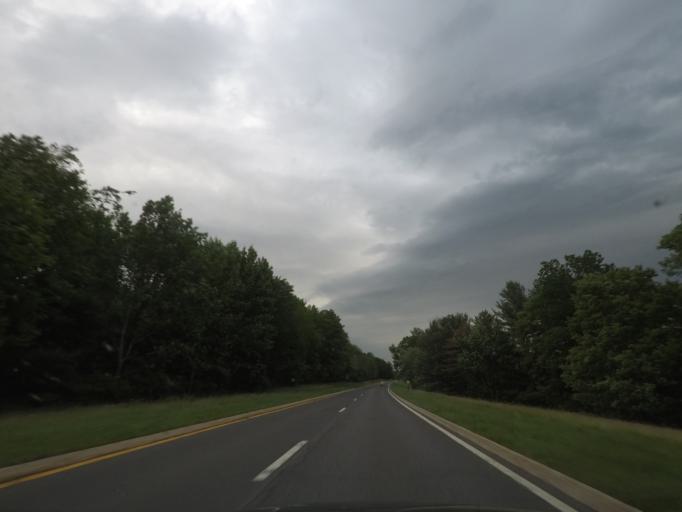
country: US
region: New York
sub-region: Columbia County
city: Philmont
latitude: 42.2436
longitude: -73.6204
